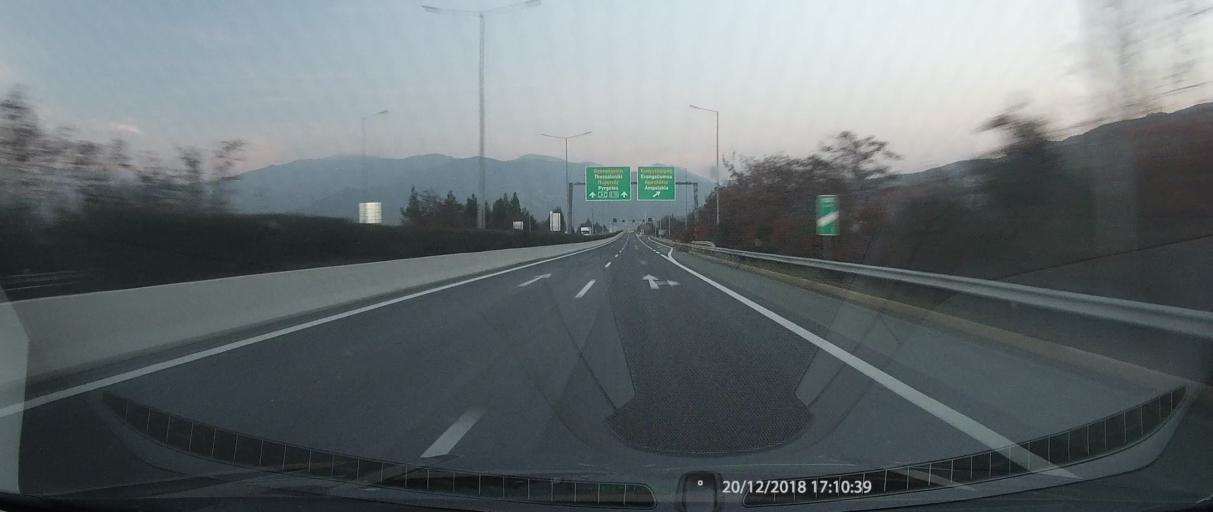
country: GR
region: Thessaly
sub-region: Nomos Larisis
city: Makrychori
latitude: 39.8237
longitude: 22.5107
